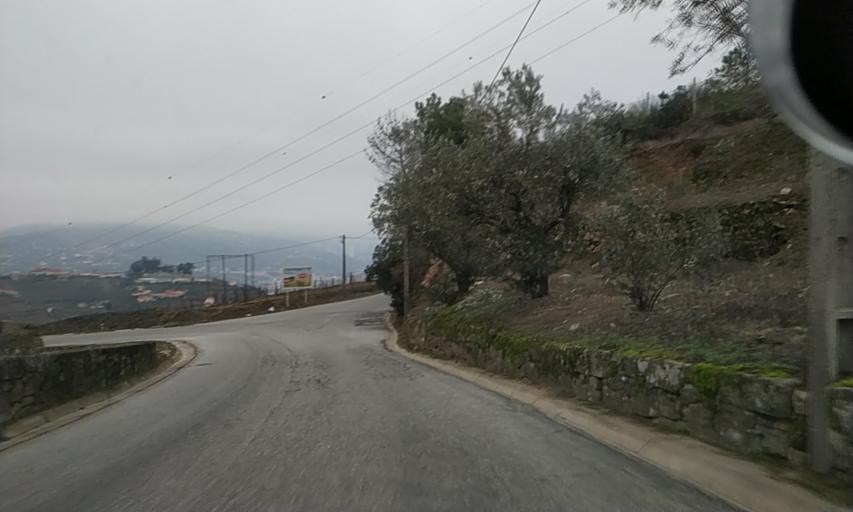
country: PT
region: Viseu
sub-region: Lamego
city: Lamego
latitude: 41.1180
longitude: -7.8027
